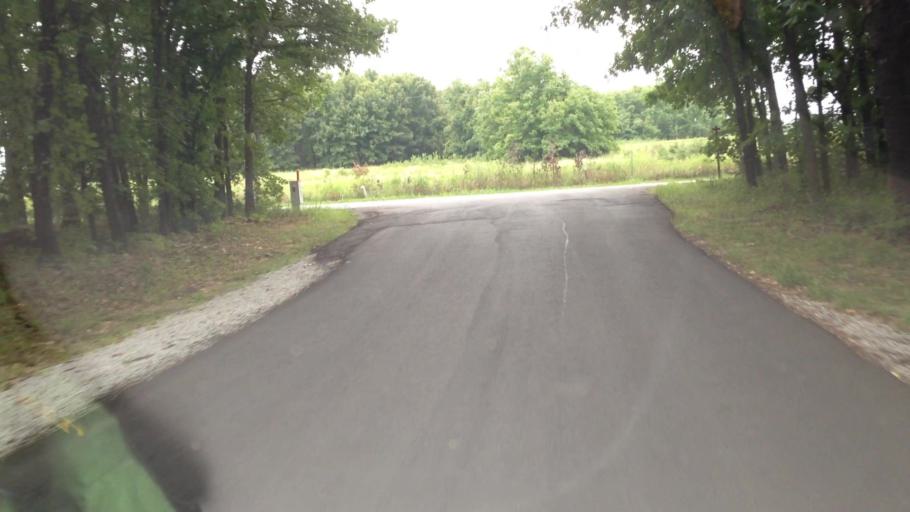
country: US
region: Oklahoma
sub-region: Delaware County
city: Cleora
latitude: 36.5469
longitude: -94.9641
